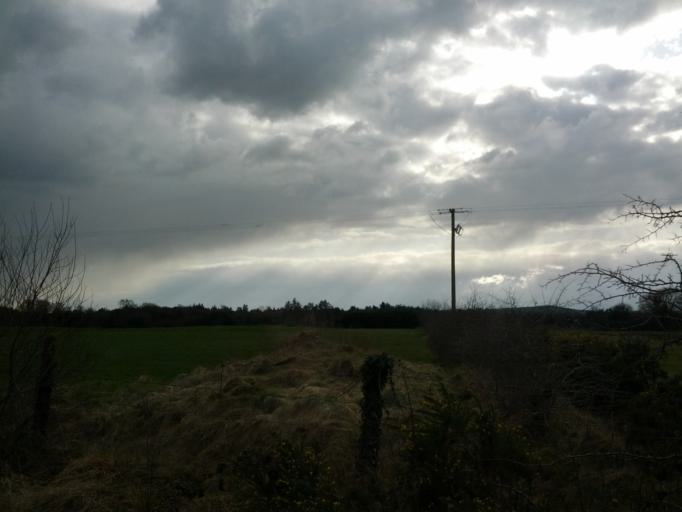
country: IE
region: Connaught
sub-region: County Galway
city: Athenry
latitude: 53.4520
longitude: -8.6955
